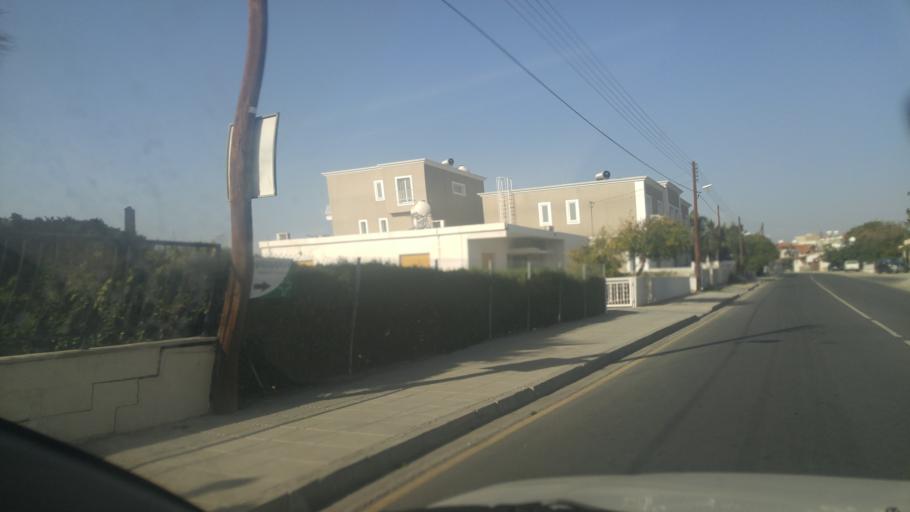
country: CY
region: Limassol
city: Pano Polemidia
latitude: 34.6907
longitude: 33.0053
